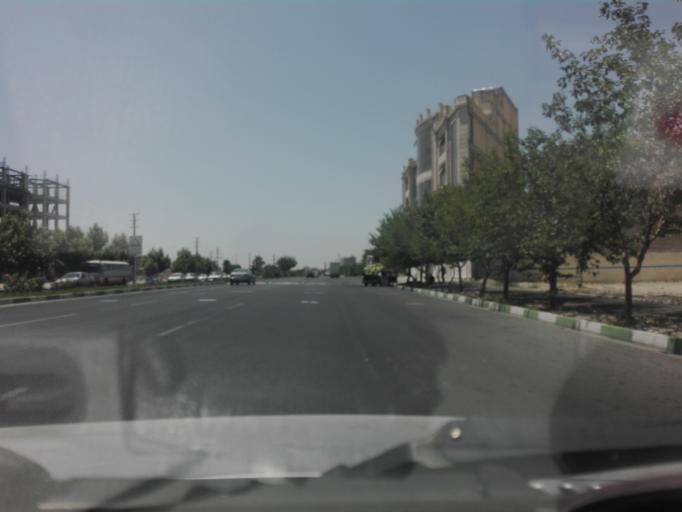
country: IR
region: Tehran
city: Malard
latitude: 35.7126
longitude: 50.9748
